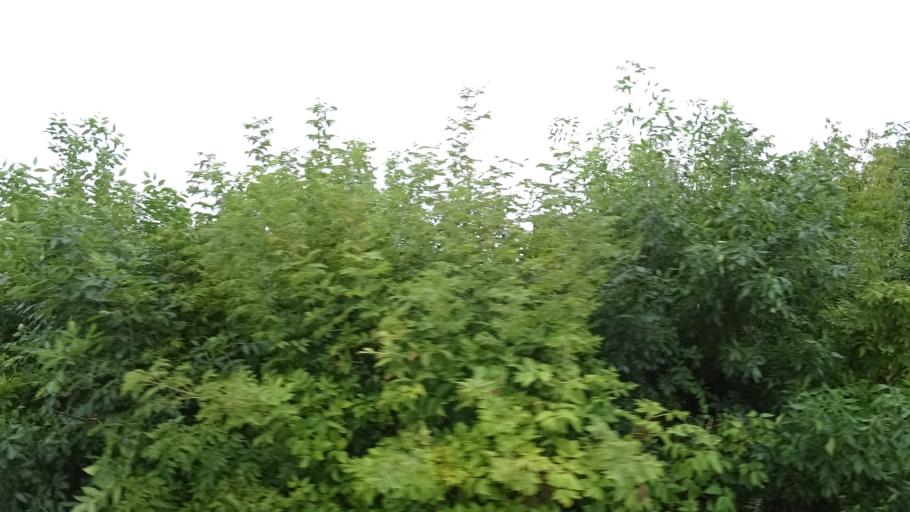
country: RU
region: Primorskiy
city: Monastyrishche
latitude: 44.2125
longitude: 132.4466
